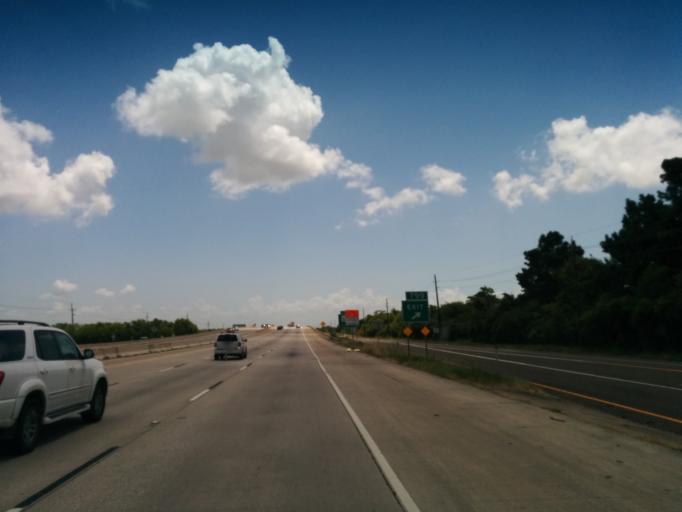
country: US
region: Texas
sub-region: Chambers County
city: Mont Belvieu
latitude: 29.8239
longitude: -94.8711
